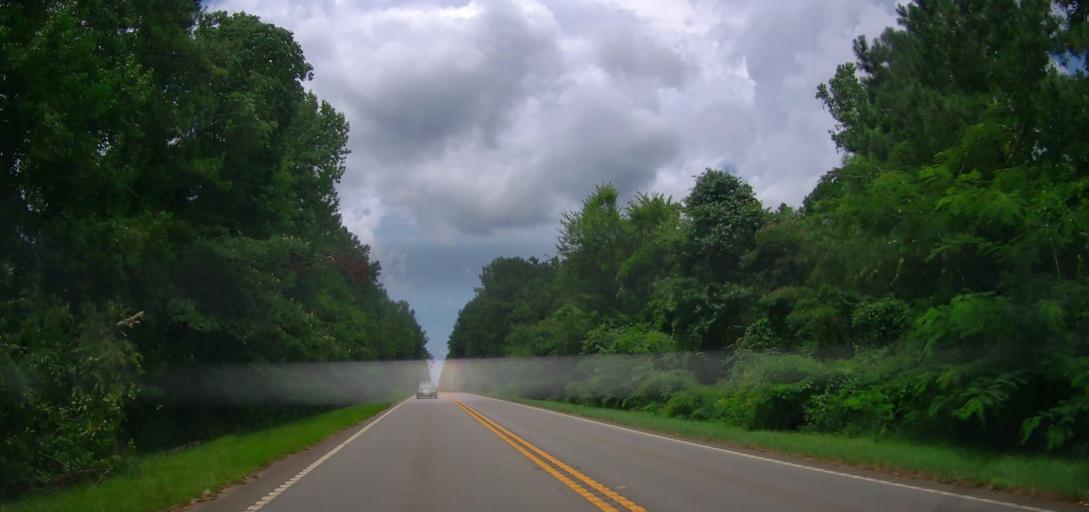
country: US
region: Georgia
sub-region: Pulaski County
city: Hawkinsville
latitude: 32.3882
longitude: -83.5562
